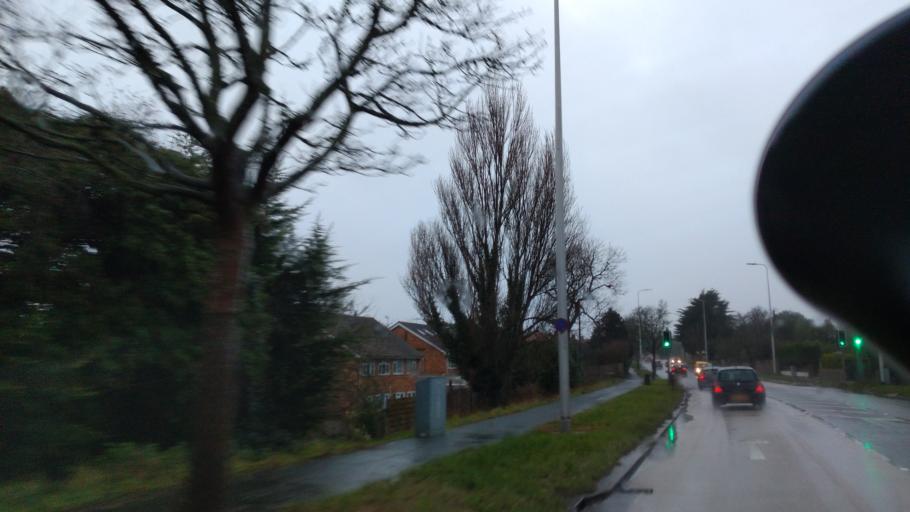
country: GB
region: England
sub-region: West Sussex
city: Findon
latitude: 50.8407
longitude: -0.4021
